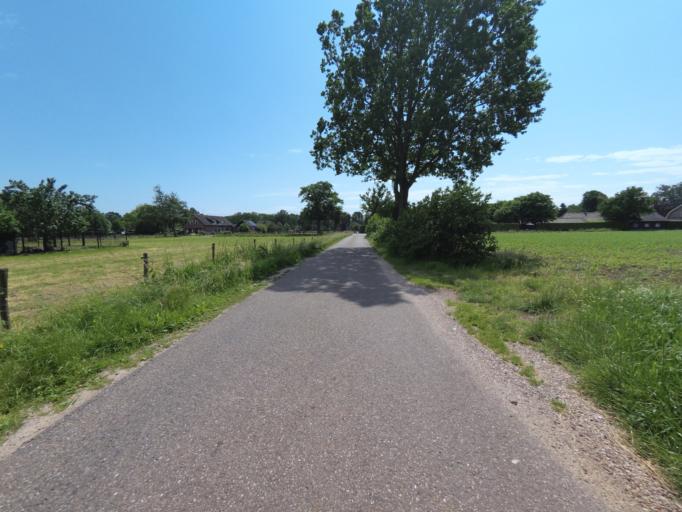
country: NL
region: Gelderland
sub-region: Gemeente Ede
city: Ederveen
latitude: 52.0610
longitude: 5.5937
